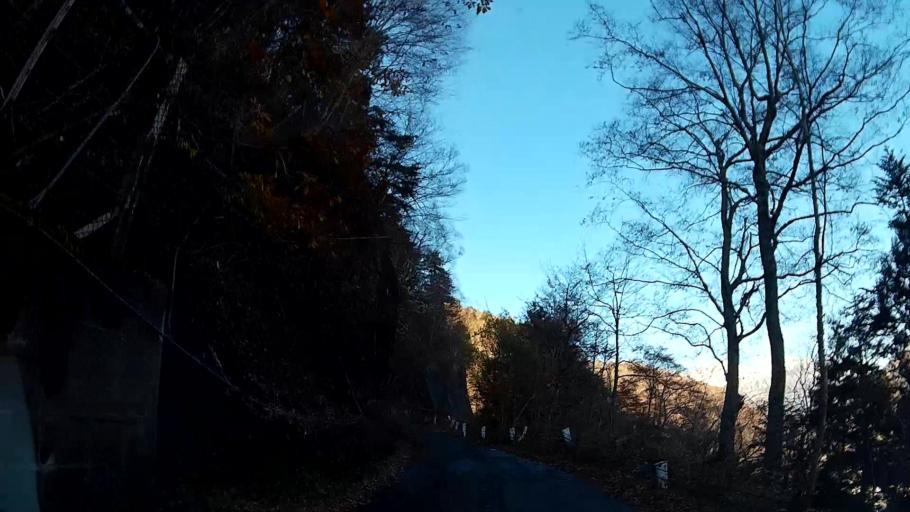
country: JP
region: Nagano
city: Hotaka
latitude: 36.2042
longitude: 137.5978
